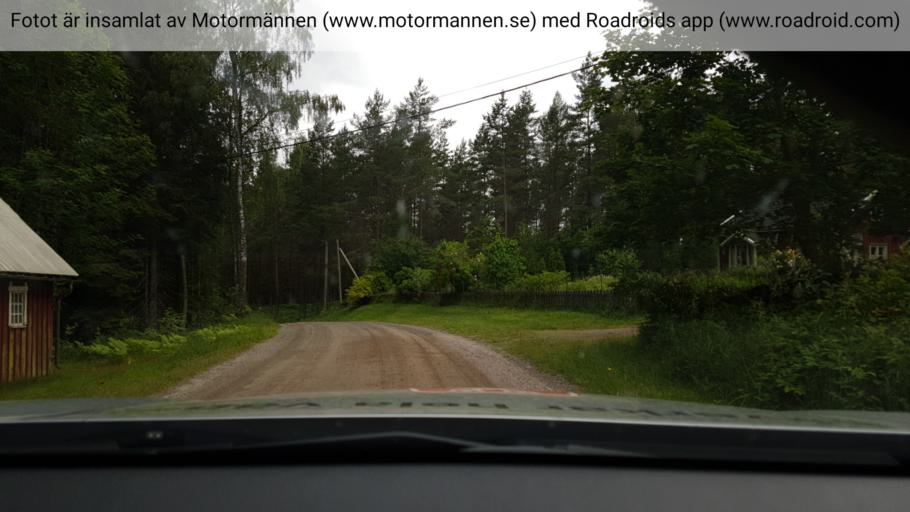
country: SE
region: Joenkoeping
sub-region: Mullsjo Kommun
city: Mullsjoe
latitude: 57.9100
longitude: 13.8001
